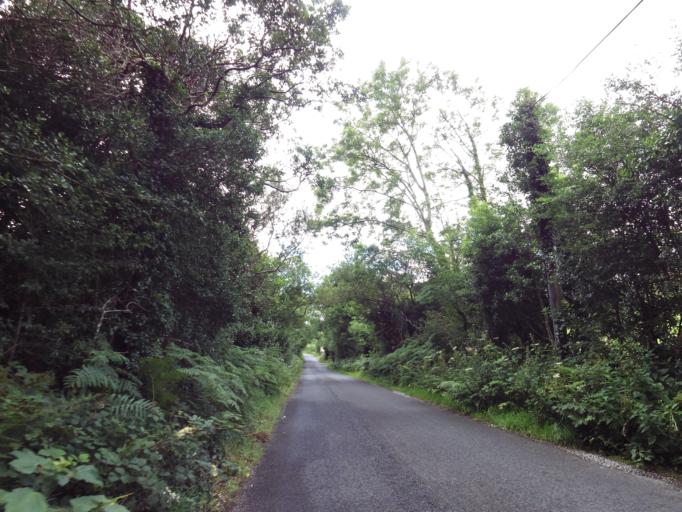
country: IE
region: Connaught
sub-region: County Galway
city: Oughterard
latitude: 53.4117
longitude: -9.3304
